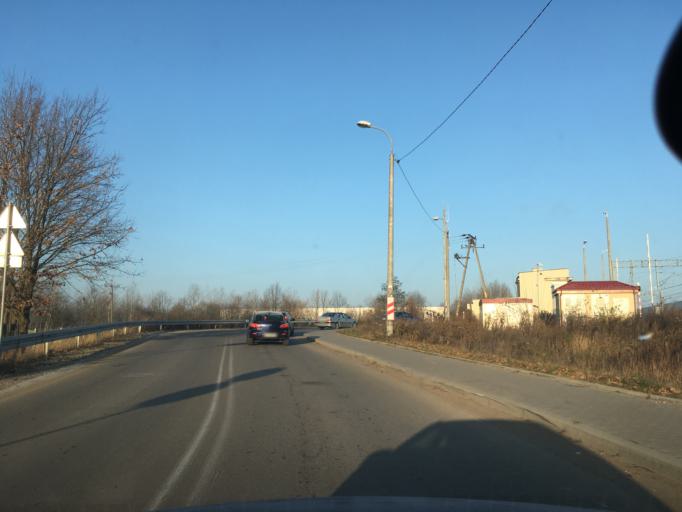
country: PL
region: Masovian Voivodeship
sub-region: Powiat piaseczynski
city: Piaseczno
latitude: 52.0733
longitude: 21.0098
